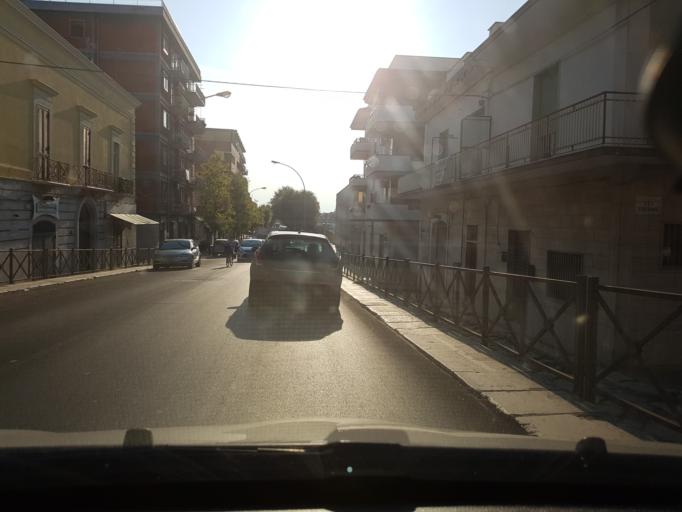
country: IT
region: Apulia
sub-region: Provincia di Foggia
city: Cerignola
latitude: 41.2655
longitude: 15.8922
